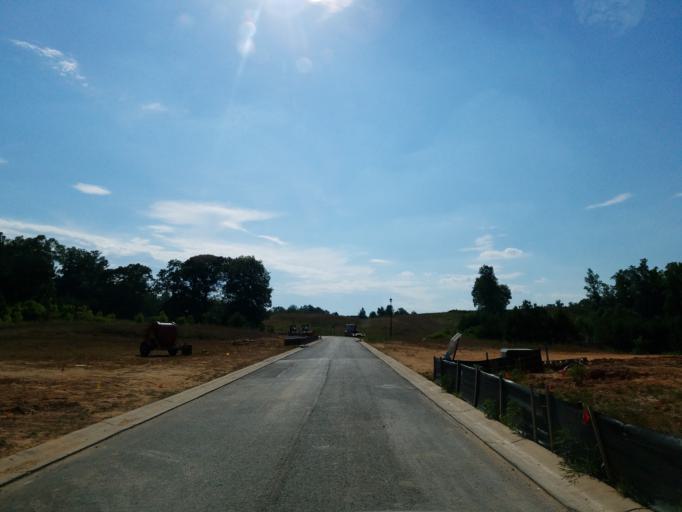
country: US
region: Georgia
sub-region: Fulton County
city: Milton
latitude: 34.1797
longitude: -84.3277
